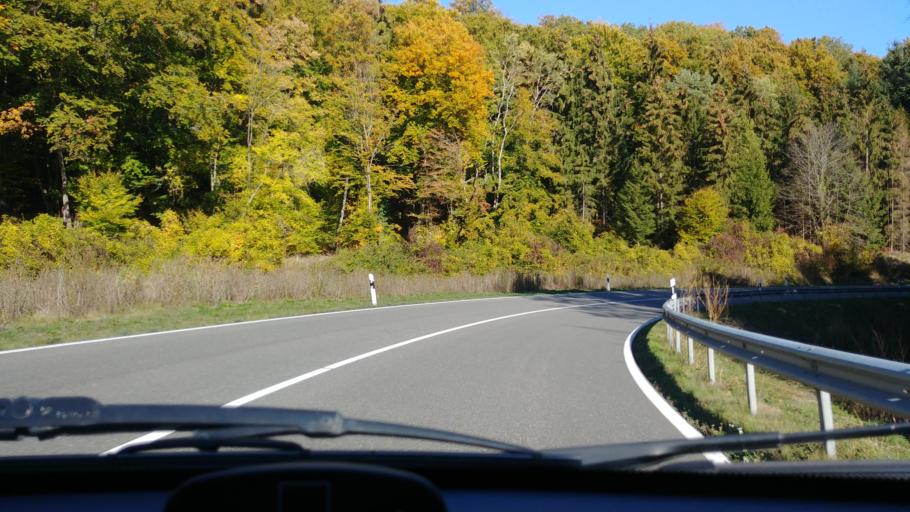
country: DE
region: Rheinland-Pfalz
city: Mudershausen
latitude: 50.2773
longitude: 8.0162
